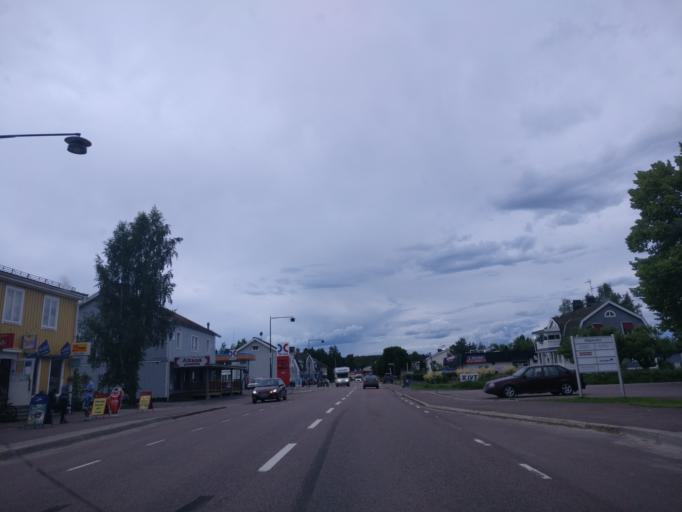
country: SE
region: Vaermland
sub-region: Hagfors Kommun
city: Ekshaerad
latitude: 60.1732
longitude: 13.4964
